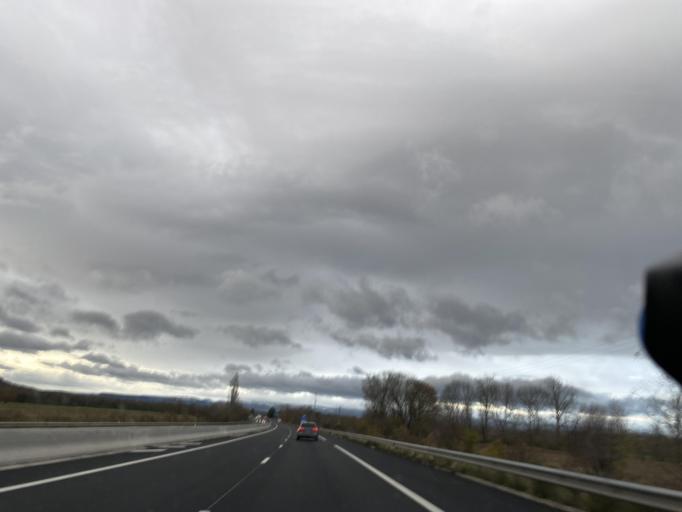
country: FR
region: Auvergne
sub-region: Departement du Puy-de-Dome
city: Culhat
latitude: 45.8389
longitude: 3.3070
